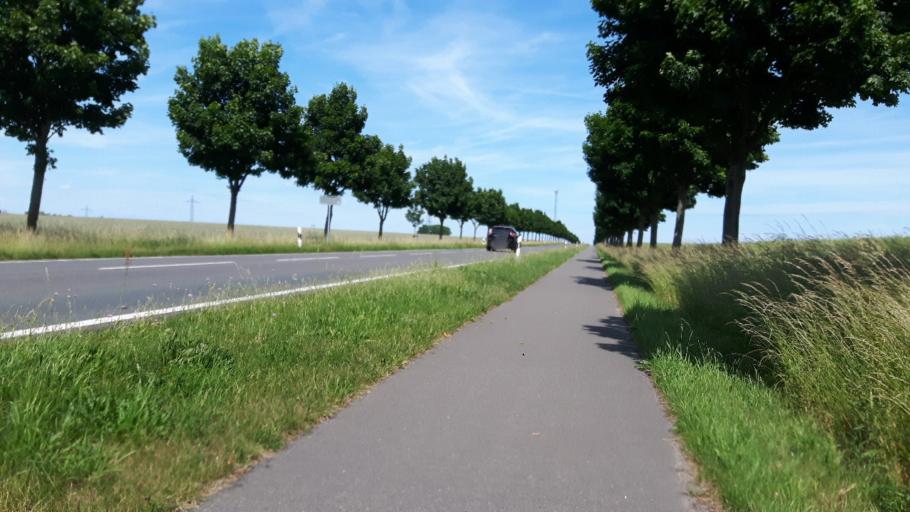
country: DE
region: Saxony-Anhalt
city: Kropstadt
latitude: 52.0171
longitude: 12.7916
